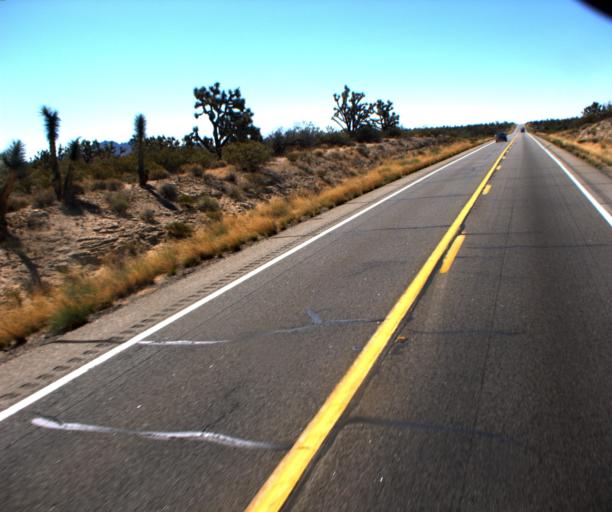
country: US
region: Arizona
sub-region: Yavapai County
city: Congress
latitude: 34.2557
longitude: -113.0852
